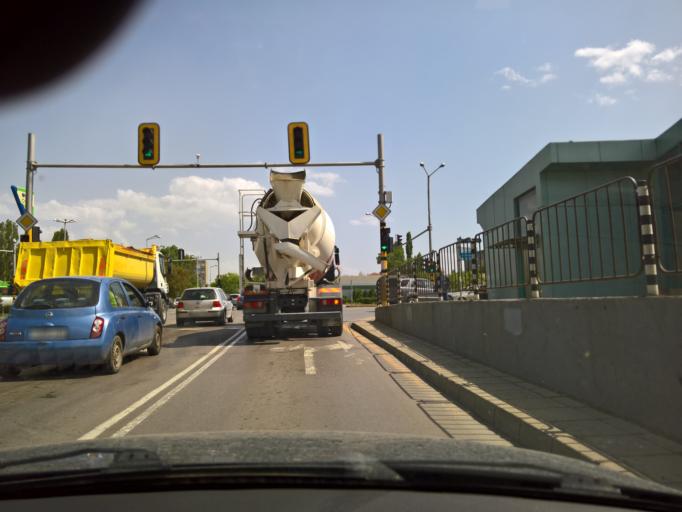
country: BG
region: Sofia-Capital
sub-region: Stolichna Obshtina
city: Sofia
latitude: 42.6633
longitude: 23.3571
